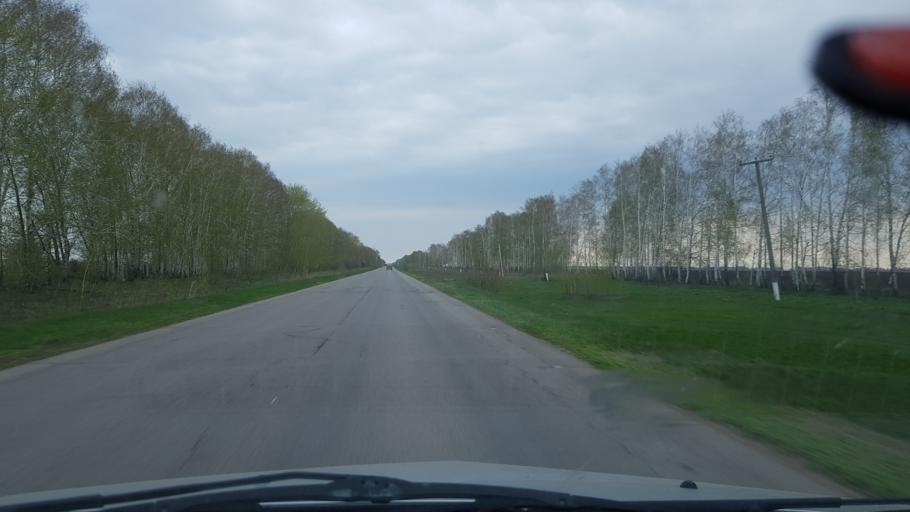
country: RU
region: Samara
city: Podstepki
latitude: 53.6602
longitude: 49.2222
